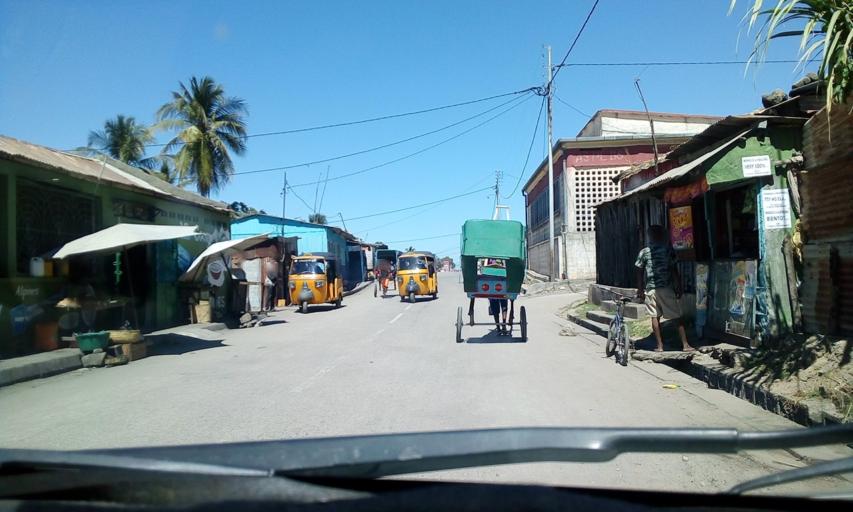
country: MG
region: Boeny
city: Mahajanga
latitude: -15.7126
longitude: 46.3220
